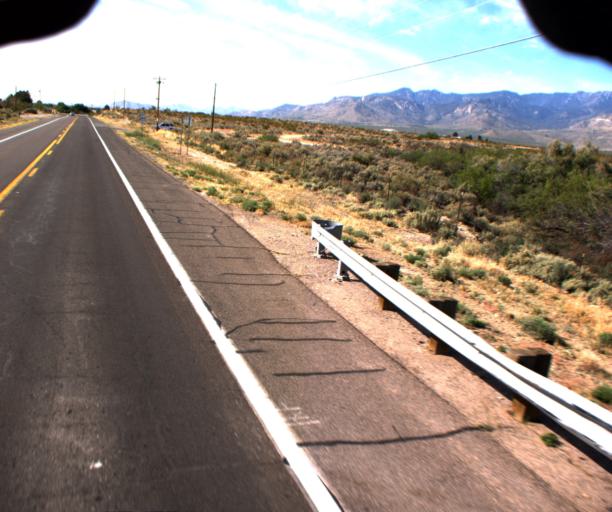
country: US
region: Arizona
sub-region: Graham County
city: Swift Trail Junction
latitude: 32.7382
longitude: -109.7163
